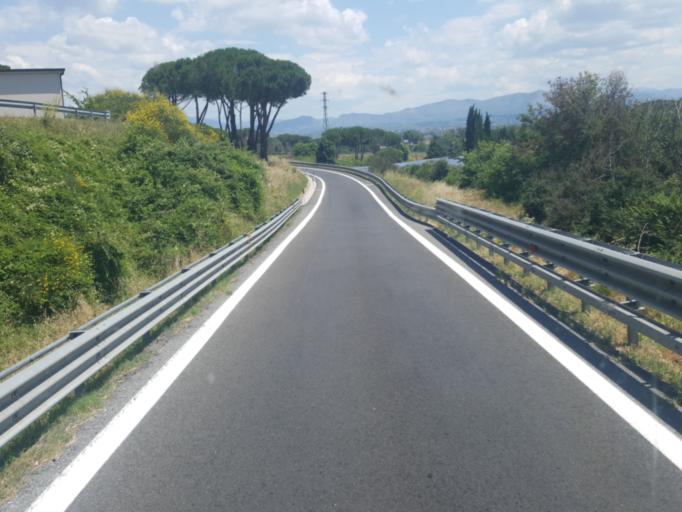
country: IT
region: Latium
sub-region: Citta metropolitana di Roma Capitale
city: Bivio di Capanelle
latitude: 42.1327
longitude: 12.6024
